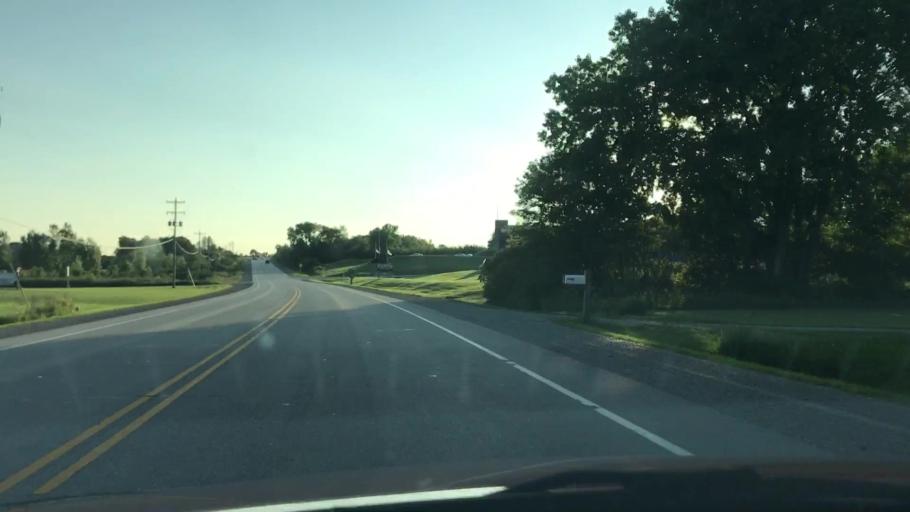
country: US
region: Wisconsin
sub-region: Brown County
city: Oneida
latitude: 44.5105
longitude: -88.1615
